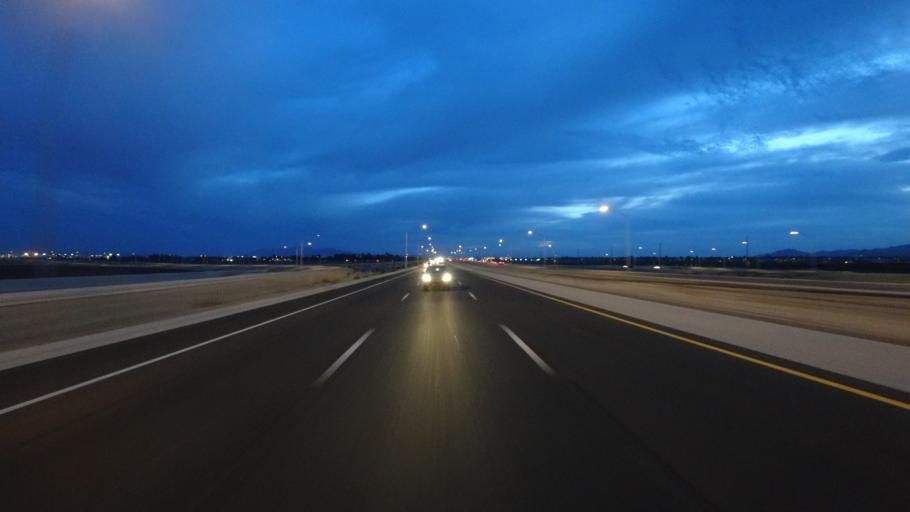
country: US
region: Arizona
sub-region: Maricopa County
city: Citrus Park
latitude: 33.5633
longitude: -112.4180
